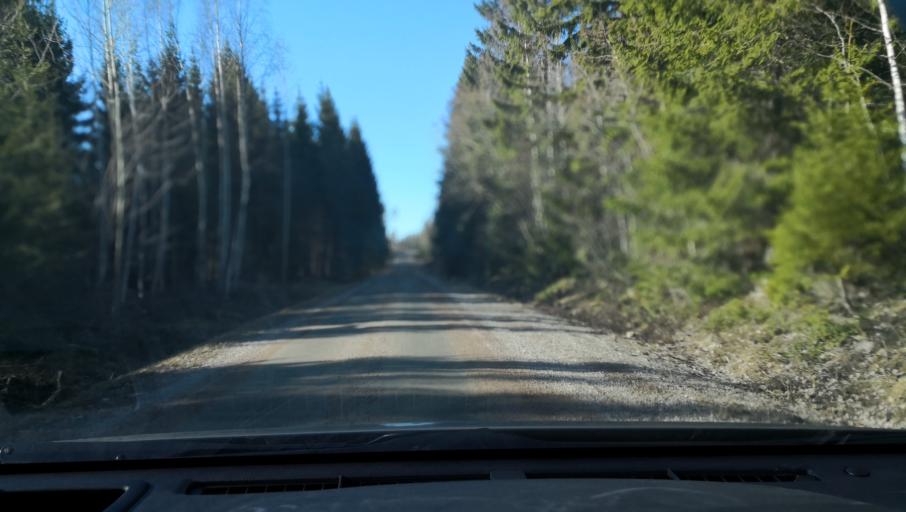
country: SE
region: Vaestmanland
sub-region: Sala Kommun
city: Sala
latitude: 60.1566
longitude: 16.6306
